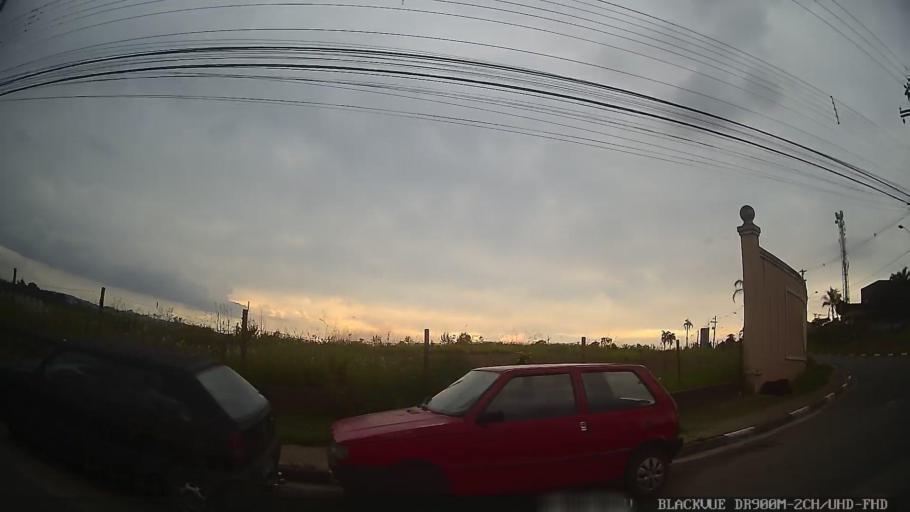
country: BR
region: Sao Paulo
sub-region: Atibaia
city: Atibaia
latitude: -23.1349
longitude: -46.5880
